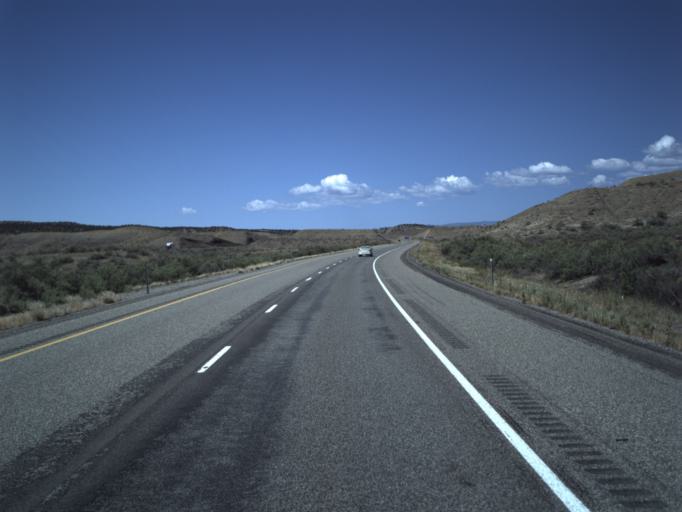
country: US
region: Colorado
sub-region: Mesa County
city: Loma
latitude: 39.1906
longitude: -109.0834
